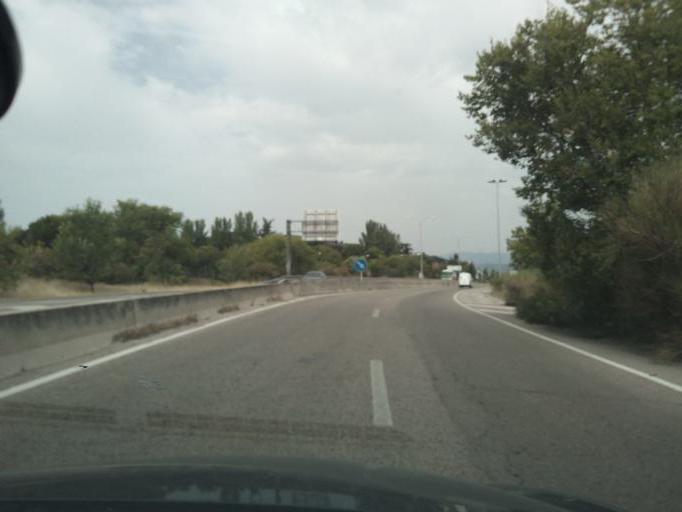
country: ES
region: Madrid
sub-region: Provincia de Madrid
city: Las Rozas de Madrid
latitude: 40.4878
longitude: -3.8697
